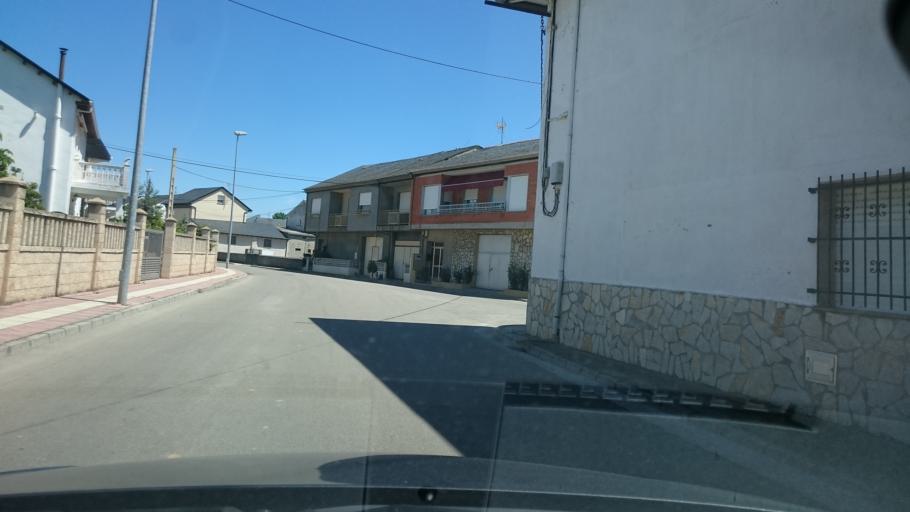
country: ES
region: Castille and Leon
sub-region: Provincia de Leon
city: Camponaraya
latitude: 42.5767
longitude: -6.6669
